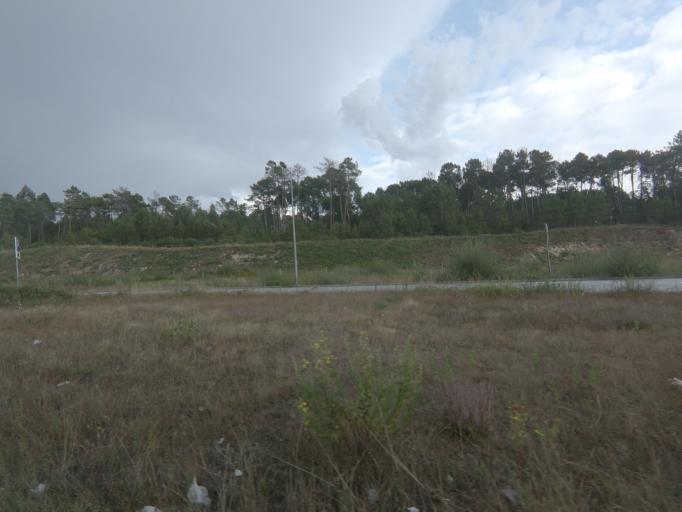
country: PT
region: Viseu
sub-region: Viseu
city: Campo
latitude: 40.7077
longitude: -7.9429
